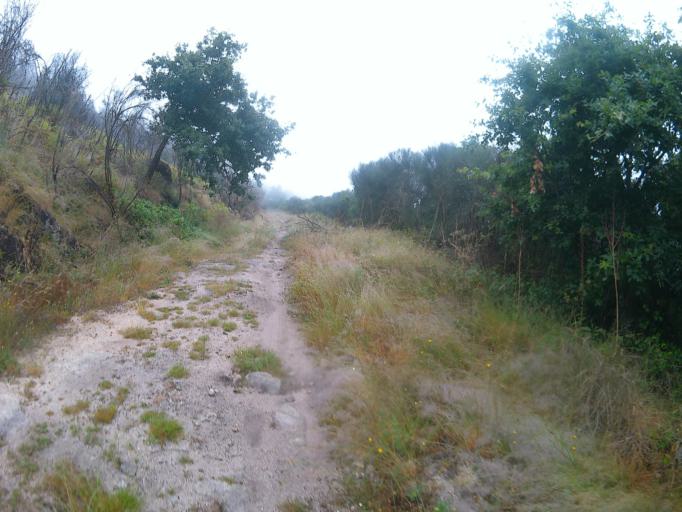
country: PT
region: Viana do Castelo
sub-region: Ponte de Lima
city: Ponte de Lima
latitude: 41.7010
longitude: -8.6058
